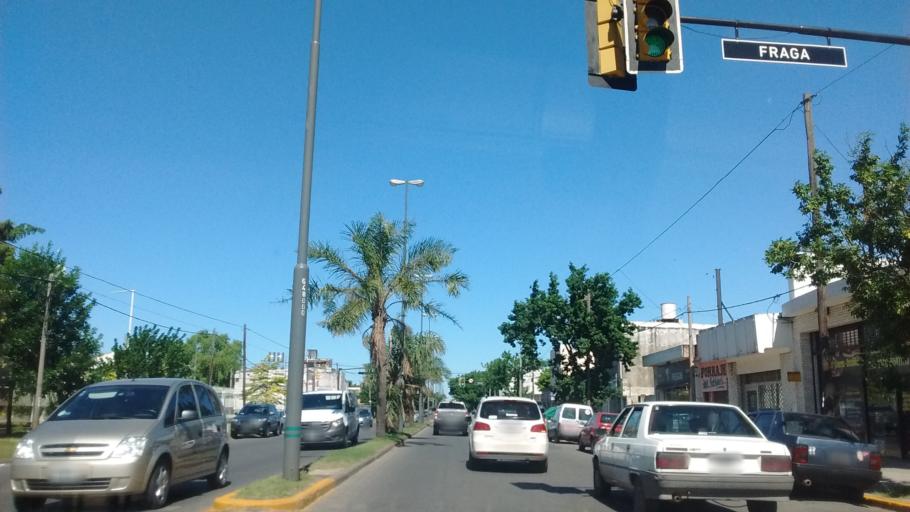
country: AR
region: Santa Fe
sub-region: Departamento de Rosario
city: Rosario
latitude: -32.9334
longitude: -60.7106
